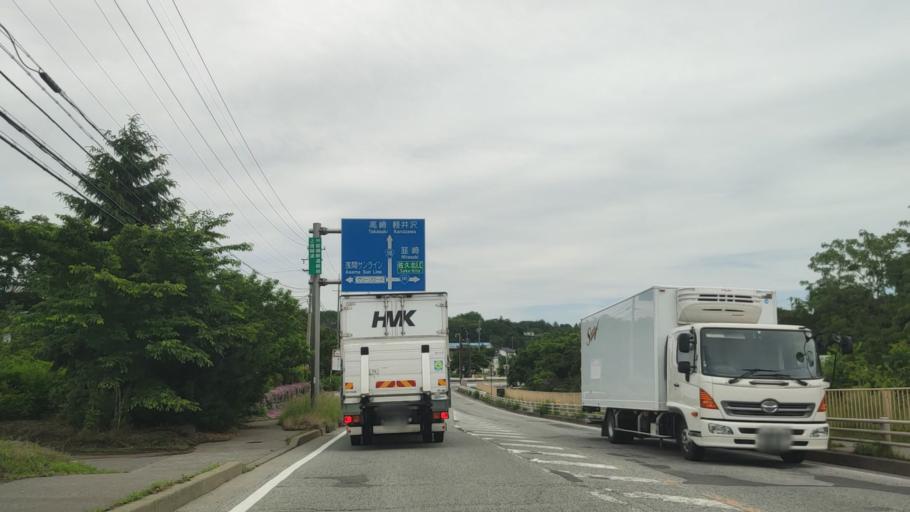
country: JP
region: Nagano
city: Komoro
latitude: 36.3136
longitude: 138.4560
